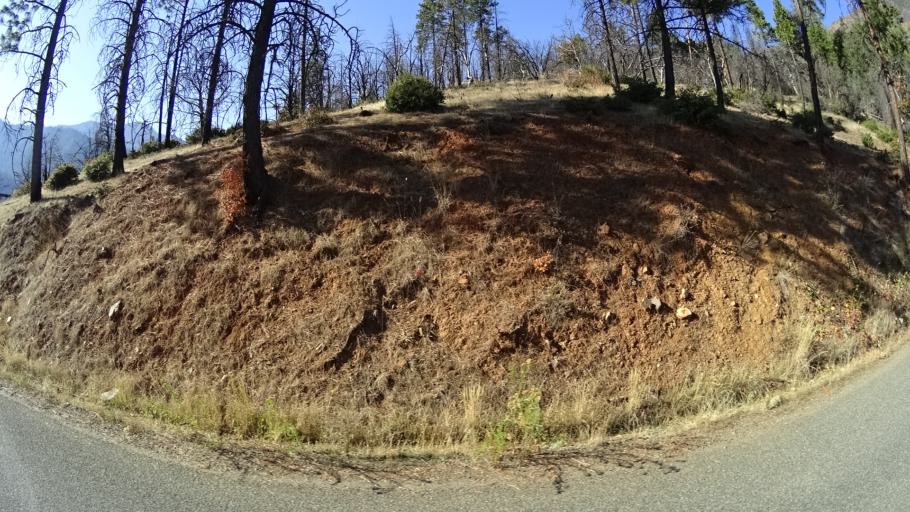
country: US
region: California
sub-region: Siskiyou County
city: Happy Camp
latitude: 41.7177
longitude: -123.0214
